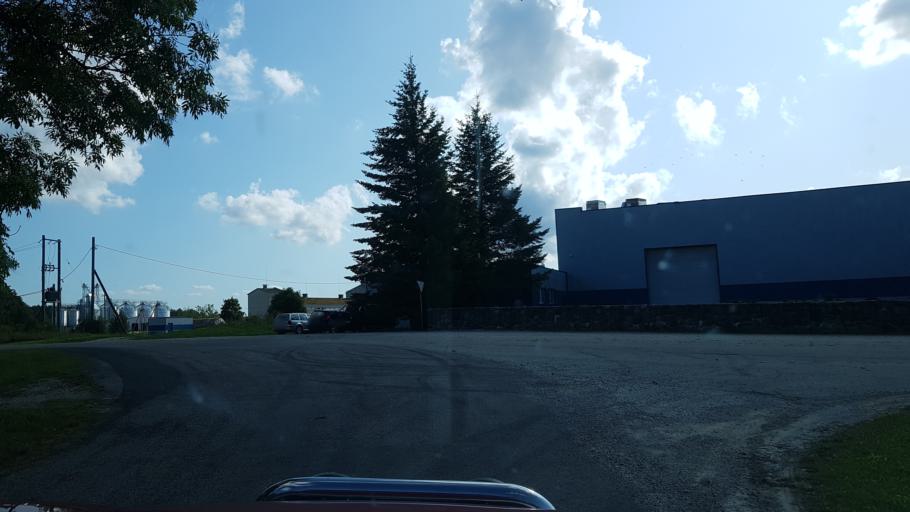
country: EE
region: Harju
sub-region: Paldiski linn
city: Paldiski
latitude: 59.2373
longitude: 24.0189
